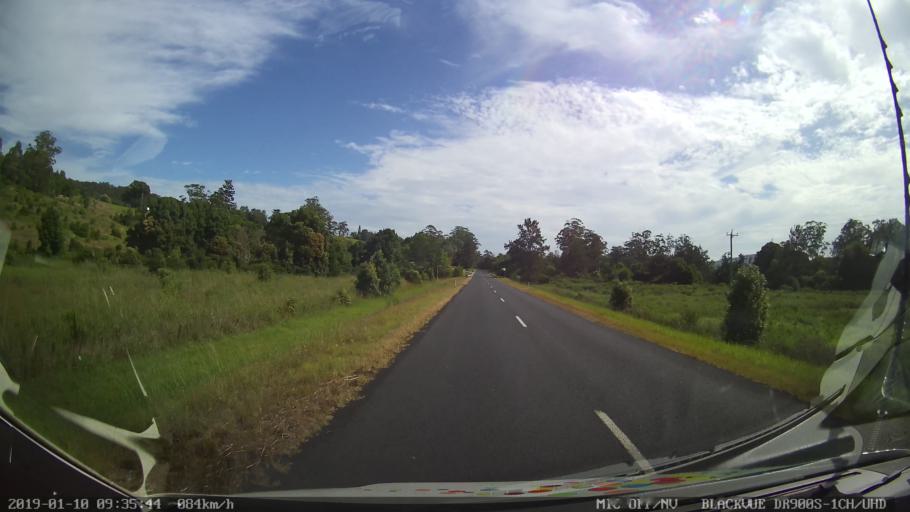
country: AU
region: New South Wales
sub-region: Coffs Harbour
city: Nana Glen
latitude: -30.2067
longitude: 153.0120
